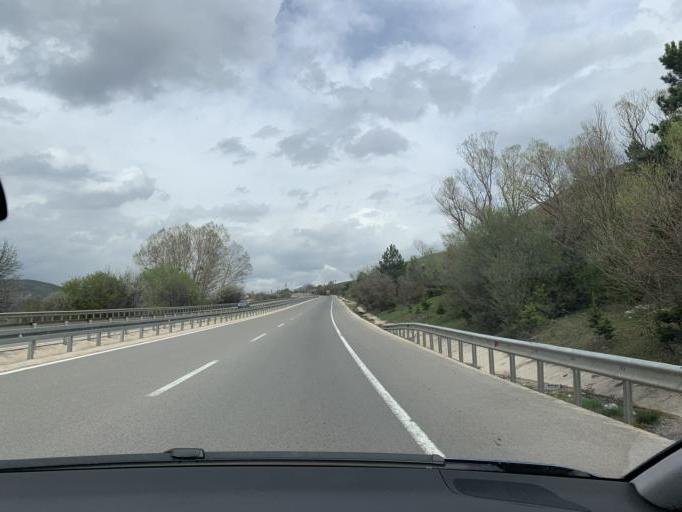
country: TR
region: Bolu
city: Gerede
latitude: 40.7868
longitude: 32.1175
